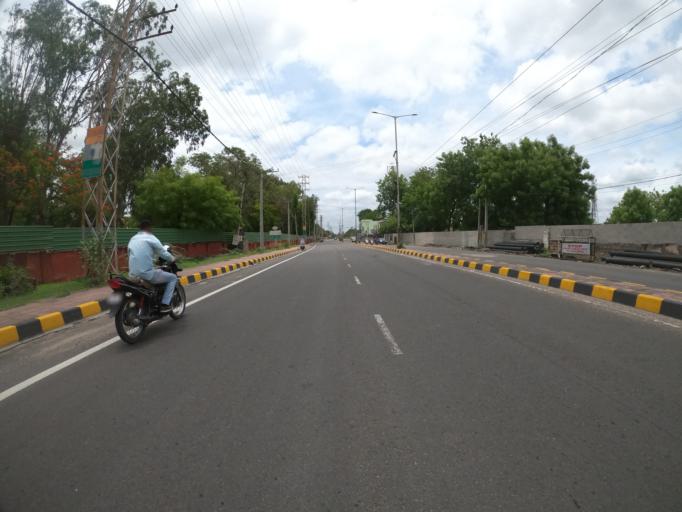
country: IN
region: Telangana
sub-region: Hyderabad
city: Hyderabad
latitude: 17.3758
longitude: 78.3942
